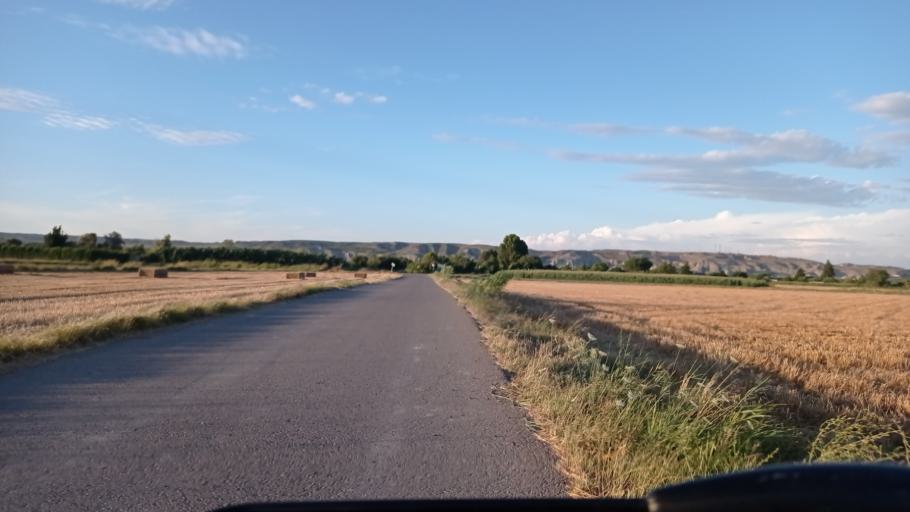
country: ES
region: Aragon
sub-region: Provincia de Zaragoza
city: Oliver-Valdefierro, Oliver, Valdefierro
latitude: 41.6827
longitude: -0.9366
